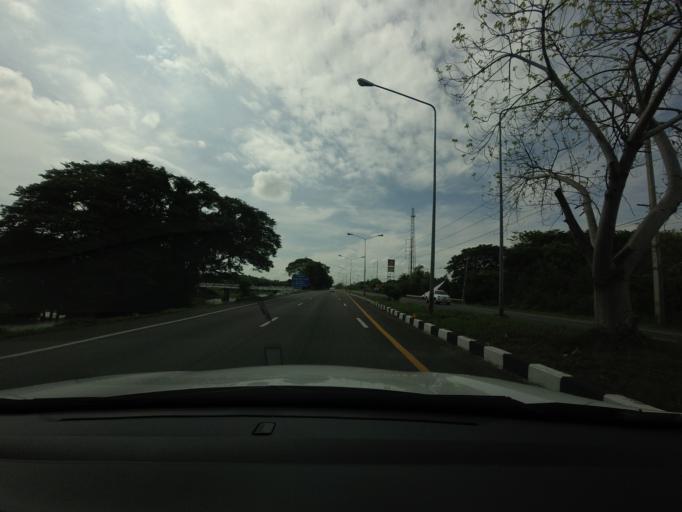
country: TH
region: Nakhon Nayok
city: Nakhon Nayok
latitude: 14.2104
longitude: 101.1787
